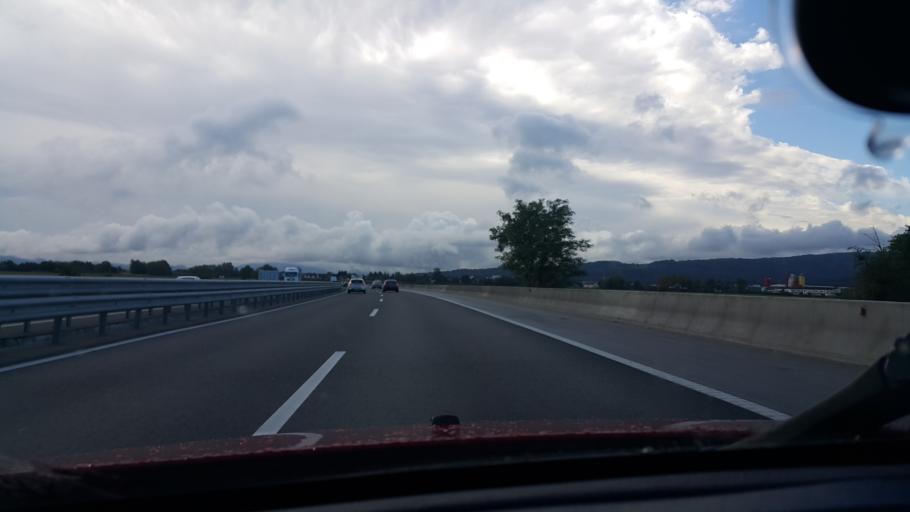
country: SI
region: Hoce-Slivnica
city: Rogoza
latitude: 46.5092
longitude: 15.6690
